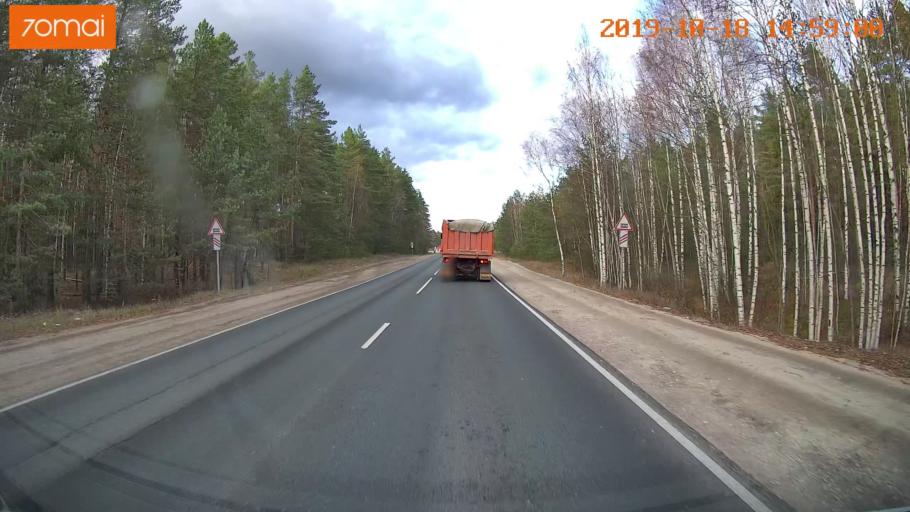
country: RU
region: Vladimir
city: Kurlovo
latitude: 55.4958
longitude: 40.5750
